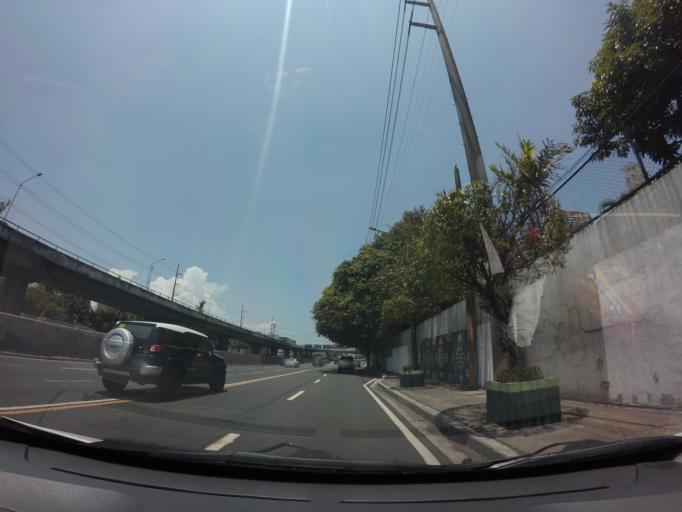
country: PH
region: Metro Manila
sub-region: Makati City
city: Makati City
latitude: 14.5521
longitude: 121.0312
